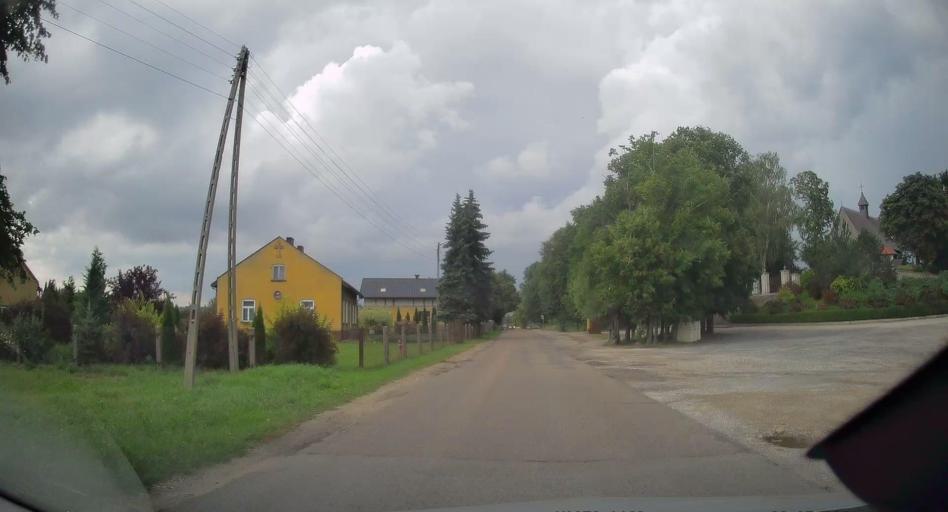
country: PL
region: Lodz Voivodeship
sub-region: Powiat rawski
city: Rawa Mazowiecka
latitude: 51.7481
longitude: 20.1869
